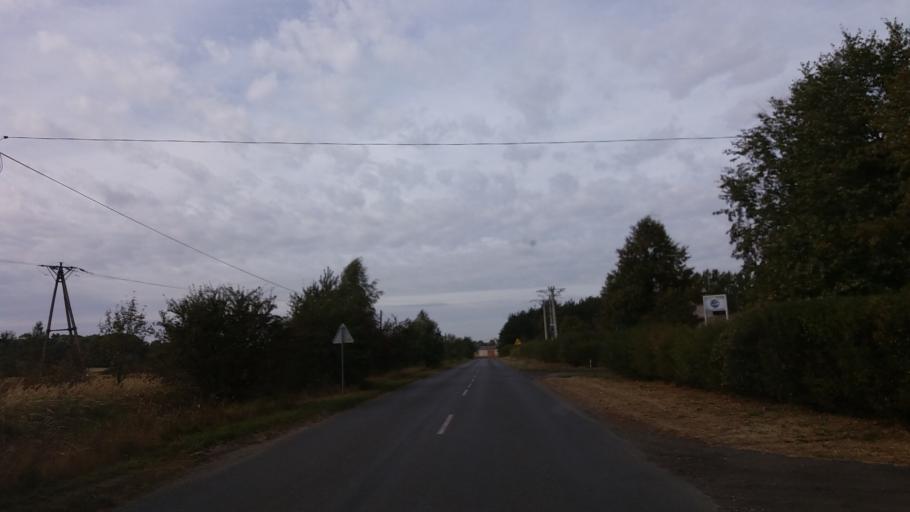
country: PL
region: Lubusz
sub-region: Powiat strzelecko-drezdenecki
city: Strzelce Krajenskie
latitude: 52.9439
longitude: 15.4583
